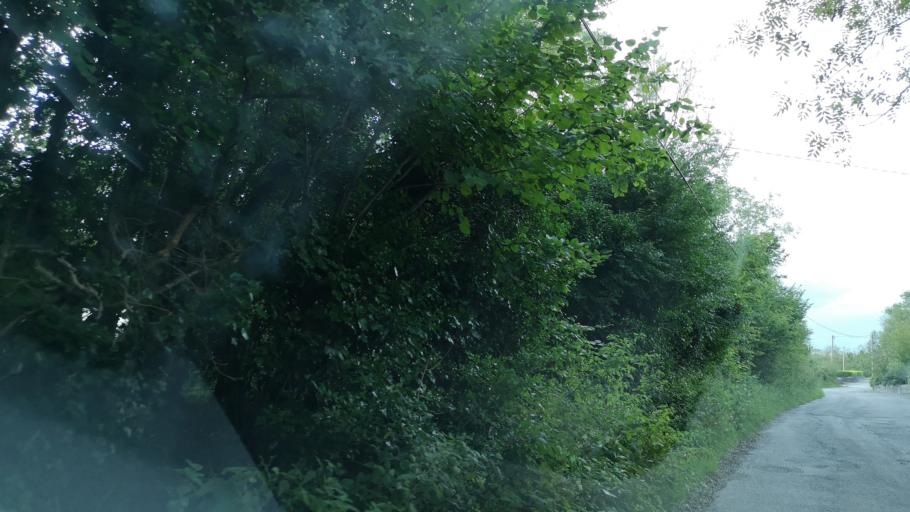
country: IE
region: Connaught
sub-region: County Galway
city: Moycullen
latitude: 53.3586
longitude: -9.1644
